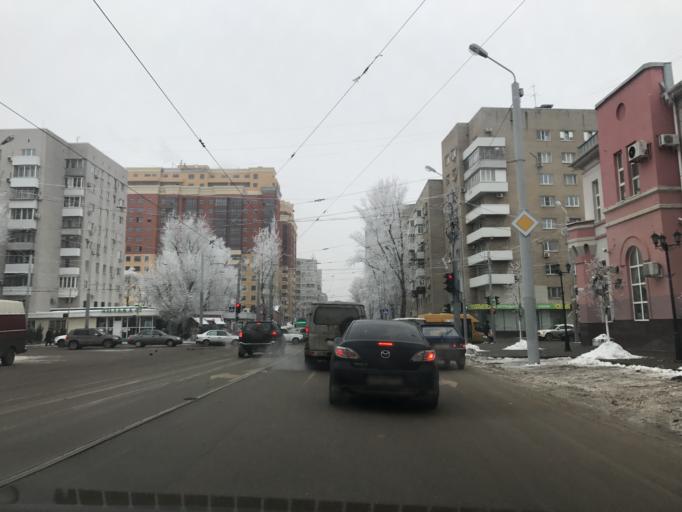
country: RU
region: Rostov
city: Rostov-na-Donu
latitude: 47.2324
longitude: 39.7409
